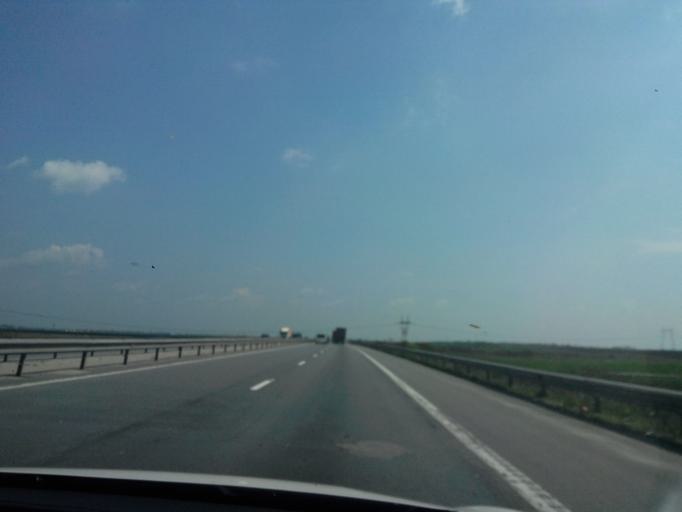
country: RO
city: Oarja Sat
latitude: 44.7781
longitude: 25.0081
